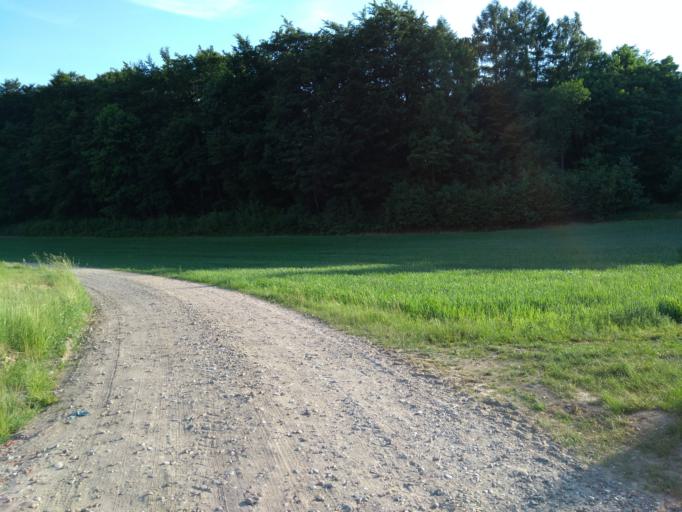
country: PL
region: Pomeranian Voivodeship
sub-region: Powiat wejherowski
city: Koleczkowo
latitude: 54.4400
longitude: 18.3258
